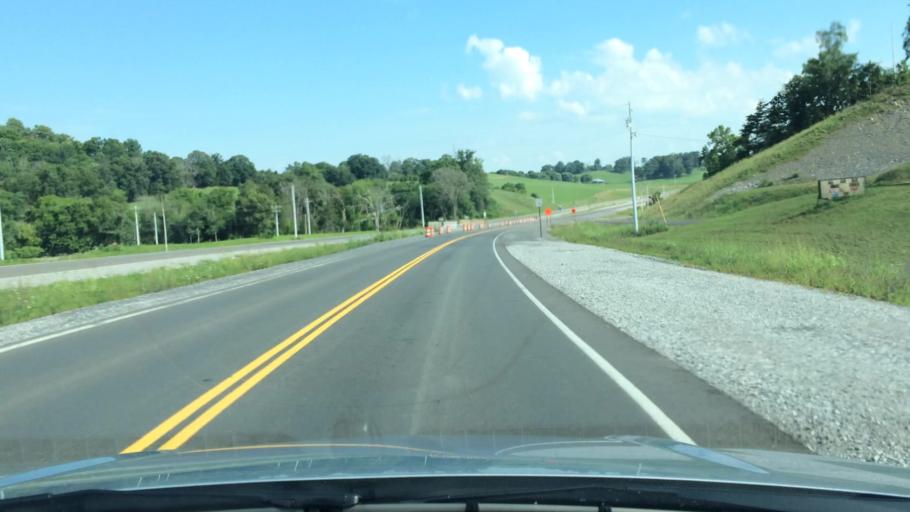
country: US
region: Tennessee
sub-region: Jefferson County
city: White Pine
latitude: 36.1401
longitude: -83.3432
